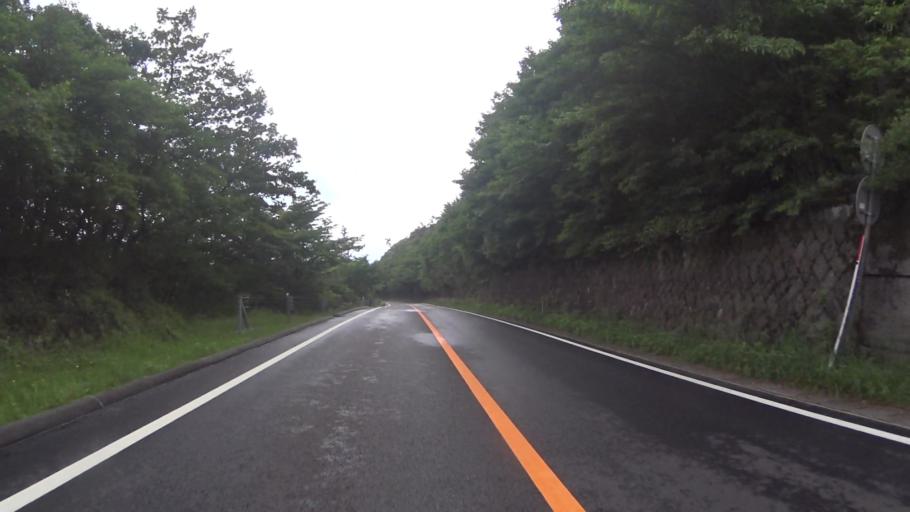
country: JP
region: Oita
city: Tsukawaki
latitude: 33.0920
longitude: 131.1978
